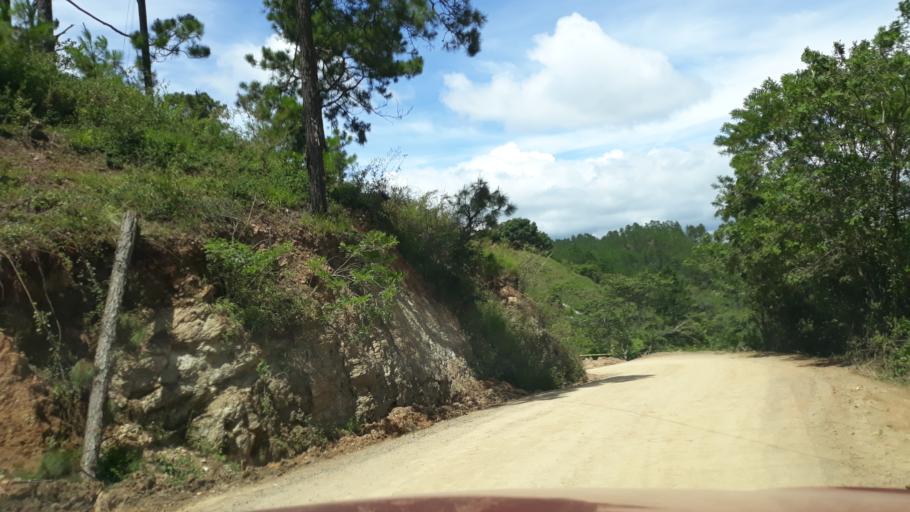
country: HN
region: El Paraiso
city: Santa Cruz
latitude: 13.7538
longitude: -86.6588
